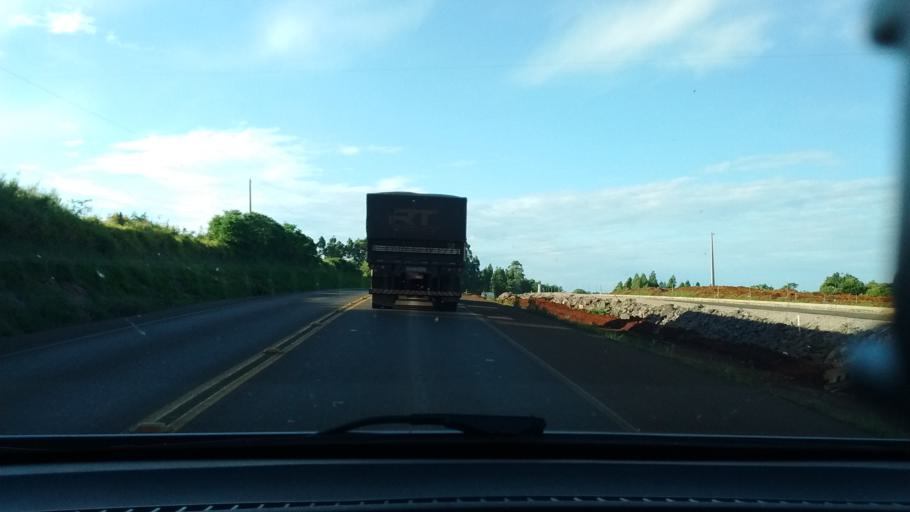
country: BR
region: Parana
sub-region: Cascavel
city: Cascavel
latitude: -25.1593
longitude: -53.5975
